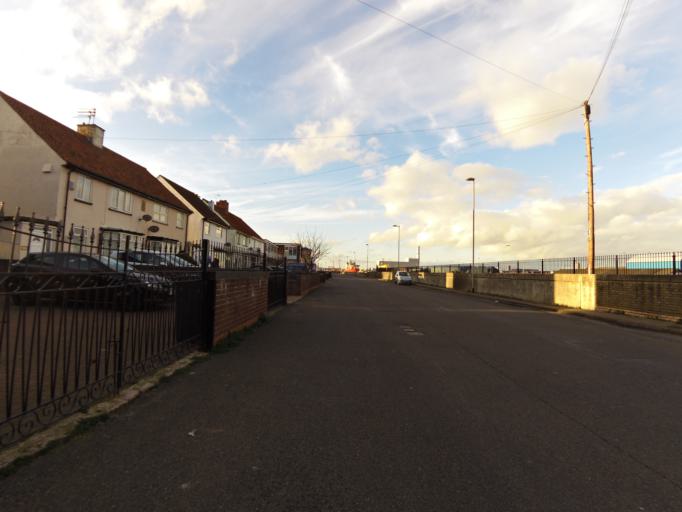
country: GB
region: England
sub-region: Norfolk
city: Gorleston-on-Sea
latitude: 52.5760
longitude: 1.7318
